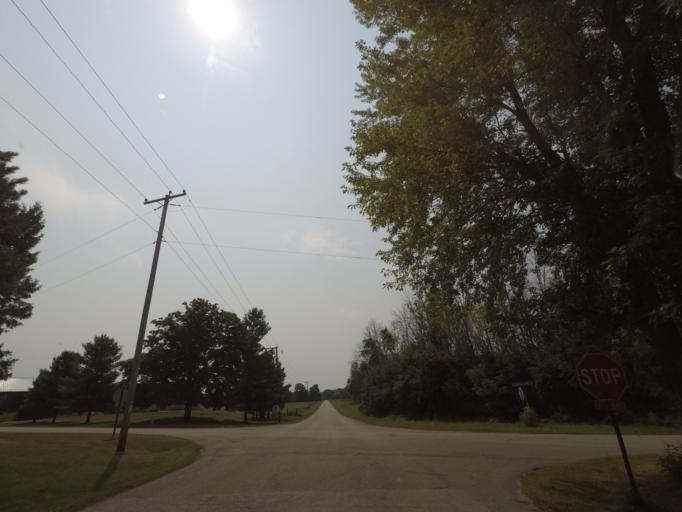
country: US
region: Wisconsin
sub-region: Waukesha County
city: Oconomowoc
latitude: 43.0665
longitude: -88.5552
